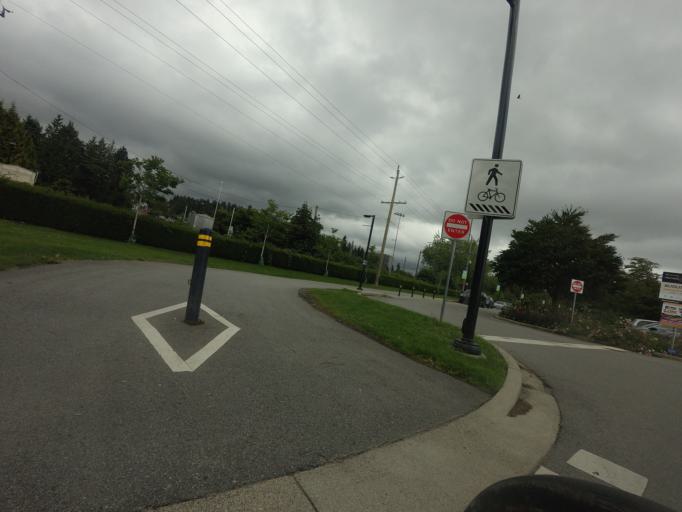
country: CA
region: British Columbia
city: West Vancouver
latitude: 49.3266
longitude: -123.1520
